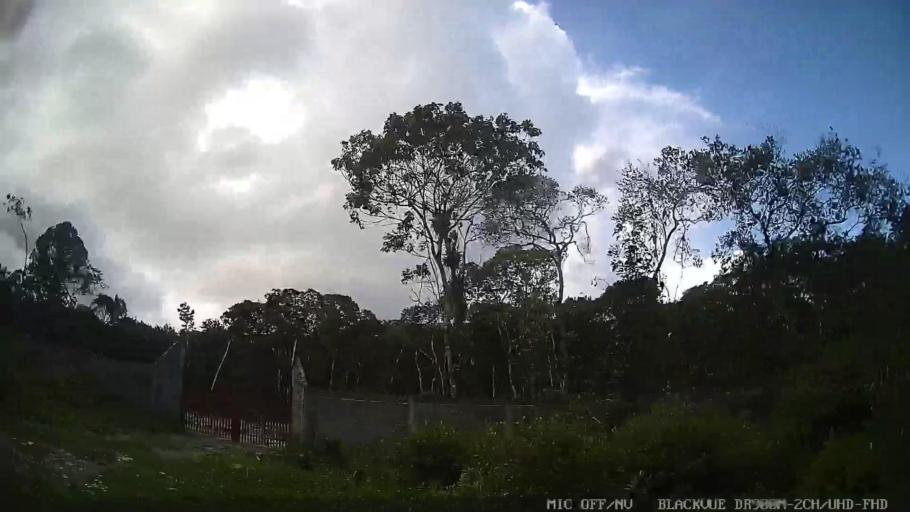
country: BR
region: Sao Paulo
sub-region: Peruibe
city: Peruibe
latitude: -24.2142
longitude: -46.9183
